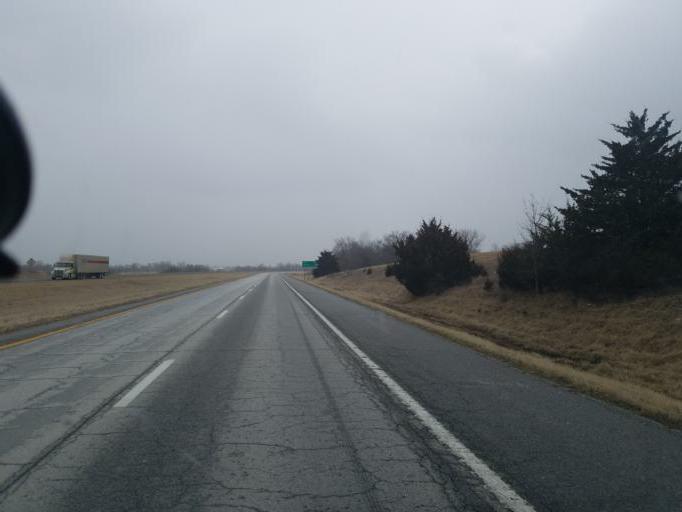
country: US
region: Missouri
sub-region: Macon County
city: La Plata
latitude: 40.0202
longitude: -92.4779
